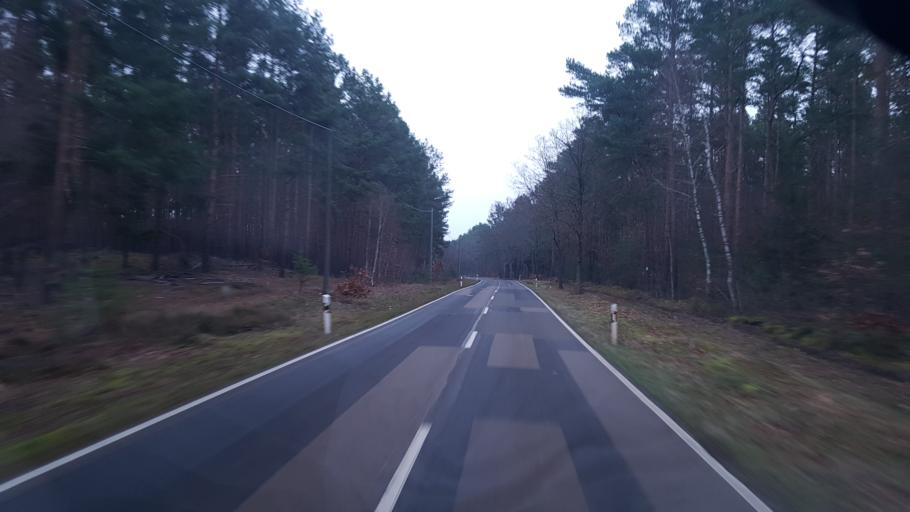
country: DE
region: Brandenburg
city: Drachhausen
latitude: 51.8761
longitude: 14.2890
